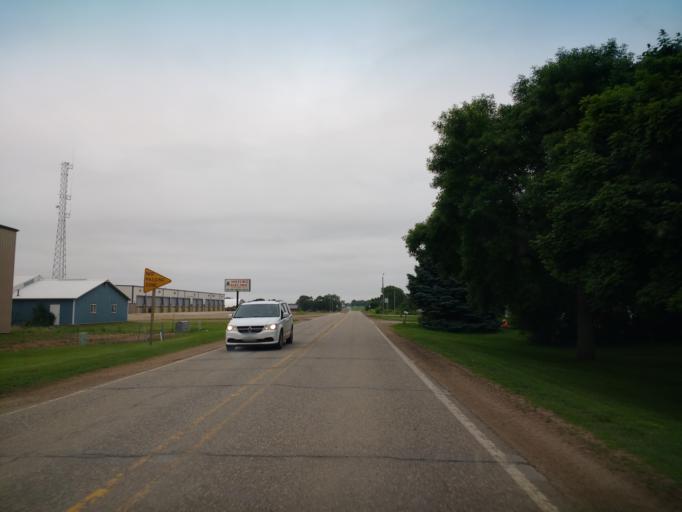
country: US
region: Iowa
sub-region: Dickinson County
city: Milford
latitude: 43.3278
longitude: -95.1436
